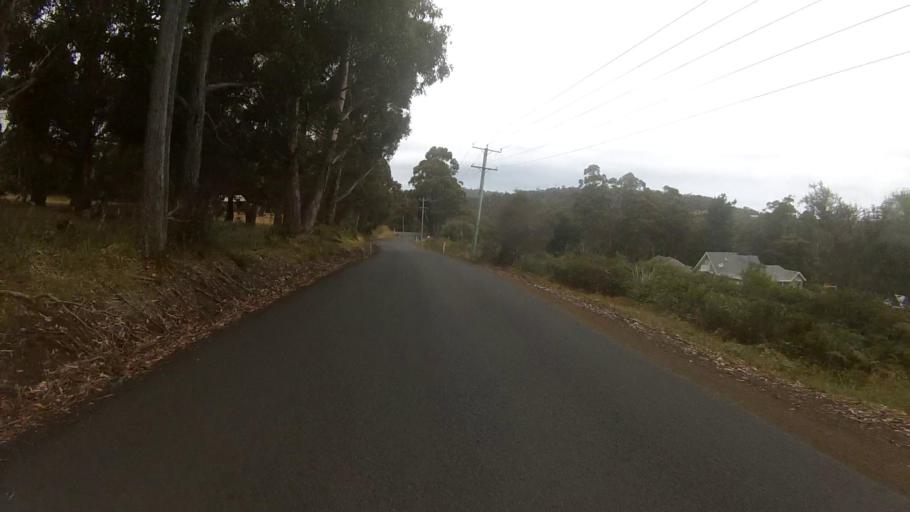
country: AU
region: Tasmania
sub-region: Kingborough
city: Margate
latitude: -42.9618
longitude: 147.2158
